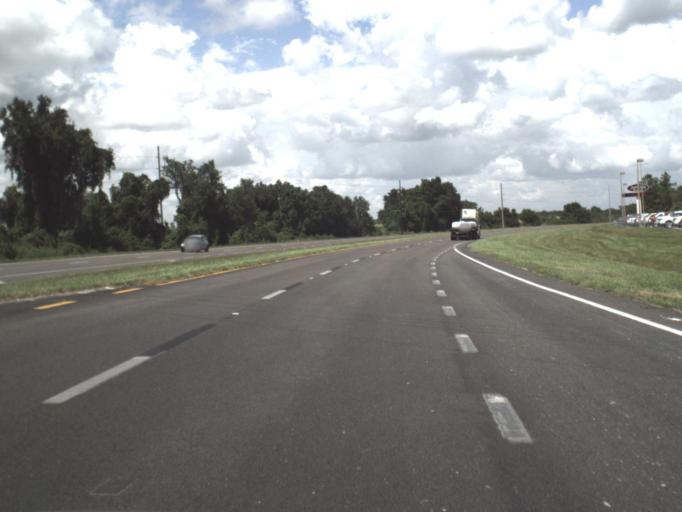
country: US
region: Florida
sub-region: Polk County
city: Fort Meade
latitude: 27.7880
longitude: -81.8122
